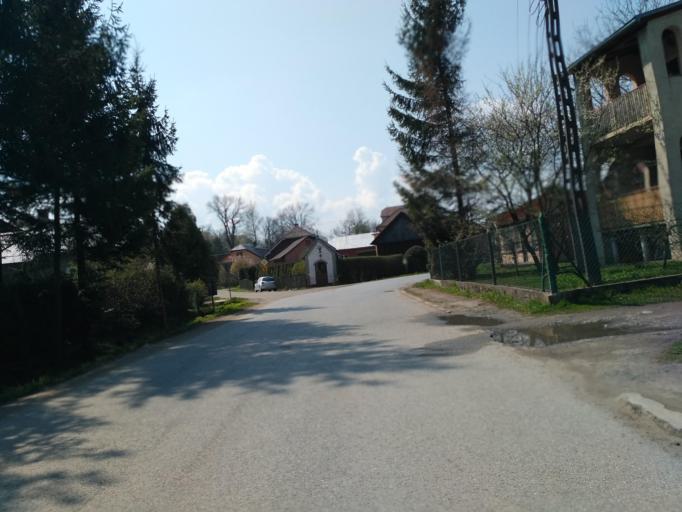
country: PL
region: Subcarpathian Voivodeship
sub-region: Powiat sanocki
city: Zarszyn
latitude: 49.5790
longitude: 22.0120
